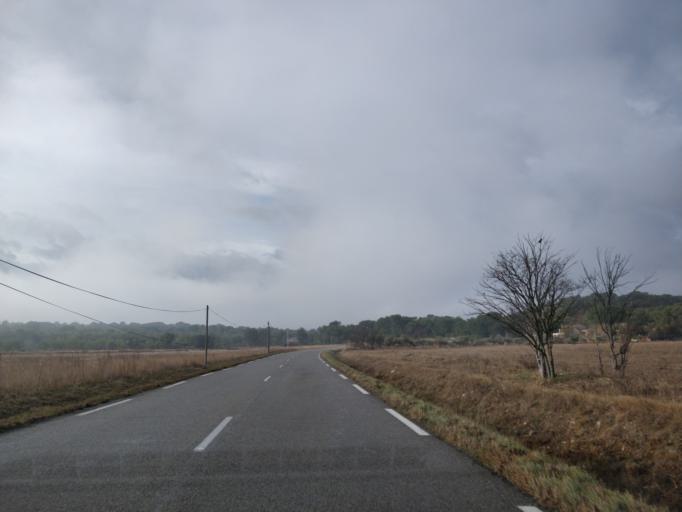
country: FR
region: Languedoc-Roussillon
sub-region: Departement du Gard
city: Nimes
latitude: 43.8697
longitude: 4.3120
